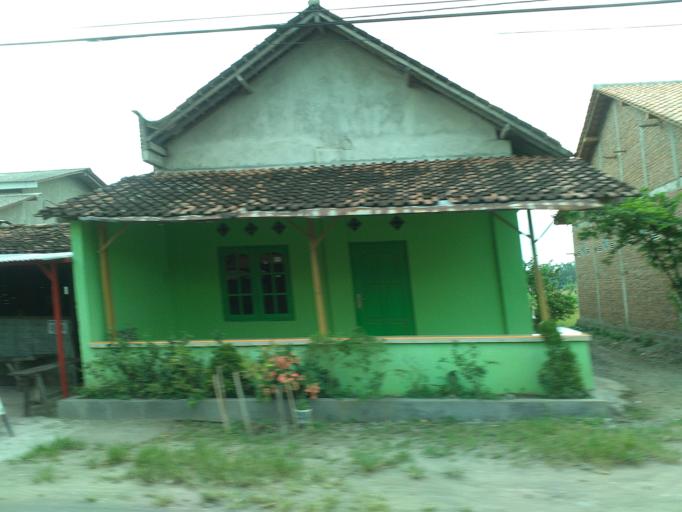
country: ID
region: Central Java
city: Ceper
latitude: -7.6628
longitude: 110.6615
